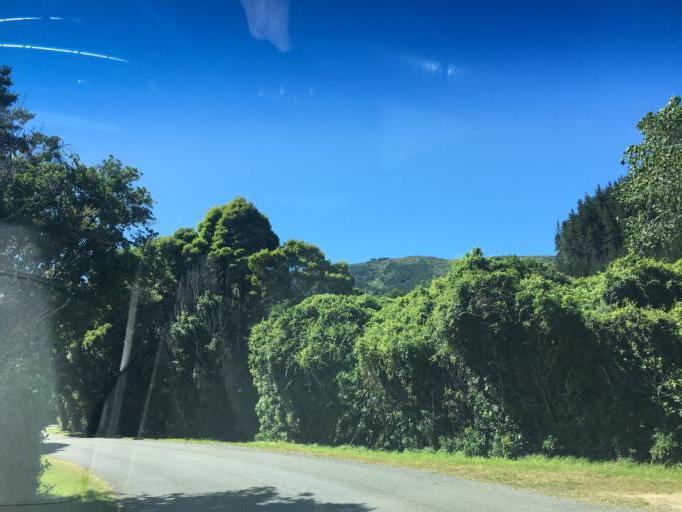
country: NZ
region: Wellington
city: Petone
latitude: -41.3541
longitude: 174.9100
